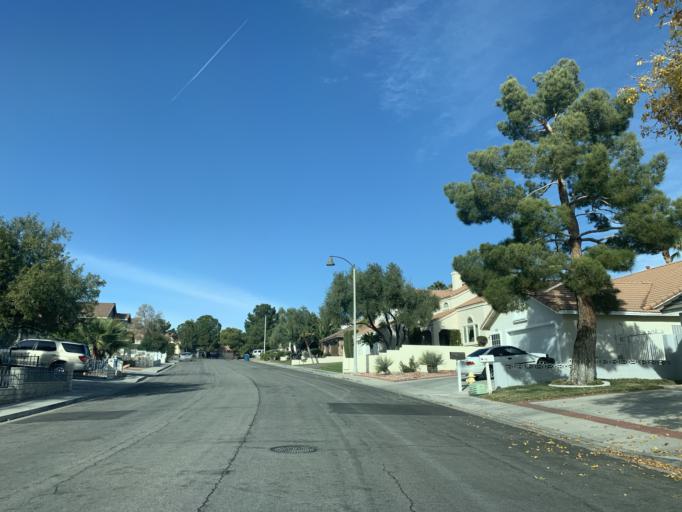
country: US
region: Nevada
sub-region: Clark County
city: Summerlin South
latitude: 36.1312
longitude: -115.2860
